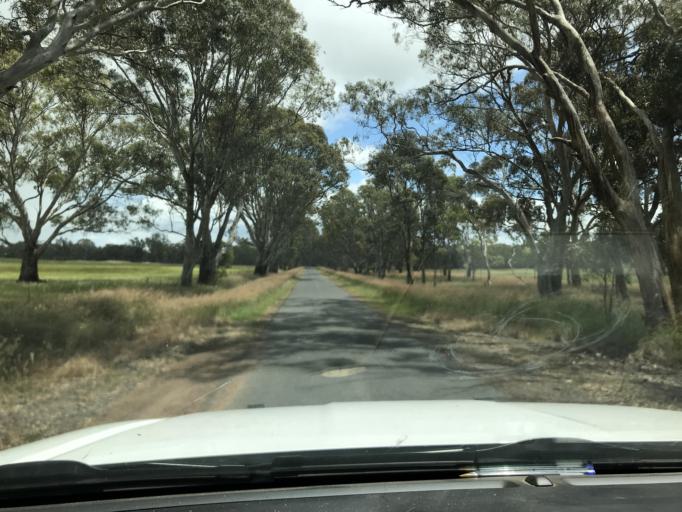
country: AU
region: Victoria
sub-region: Horsham
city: Horsham
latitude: -37.1202
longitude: 141.6835
